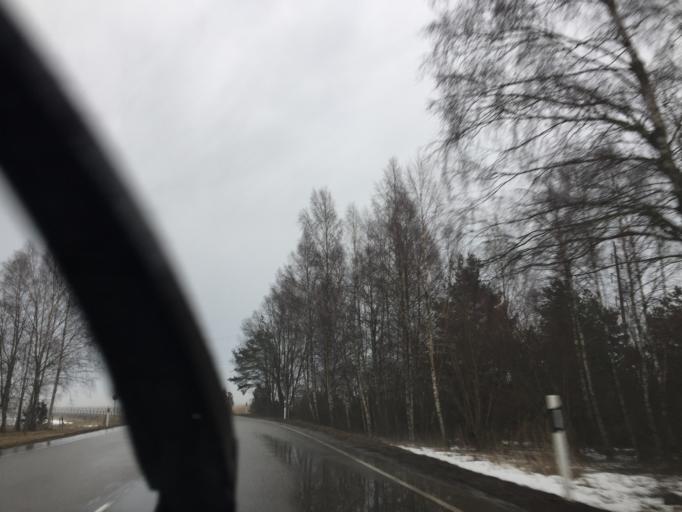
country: EE
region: Saare
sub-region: Orissaare vald
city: Orissaare
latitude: 58.5486
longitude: 23.1229
